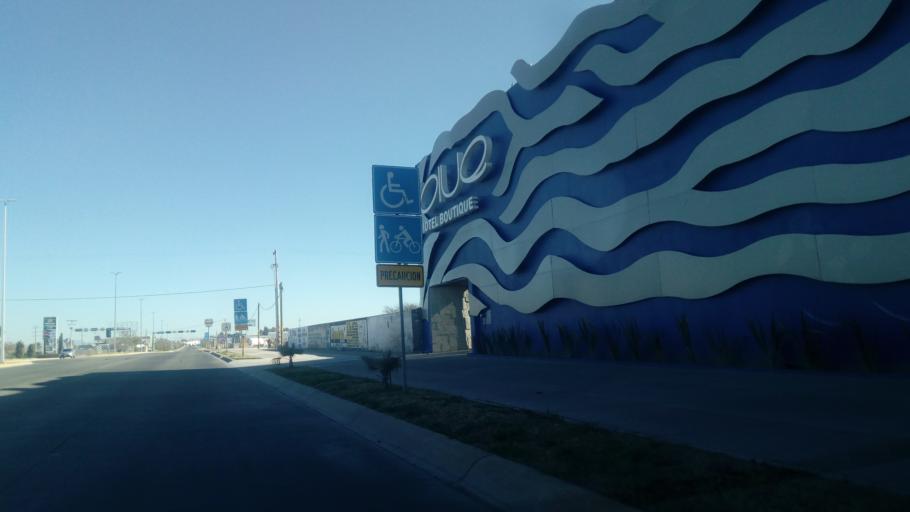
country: MX
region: Durango
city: Victoria de Durango
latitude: 24.0841
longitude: -104.5846
